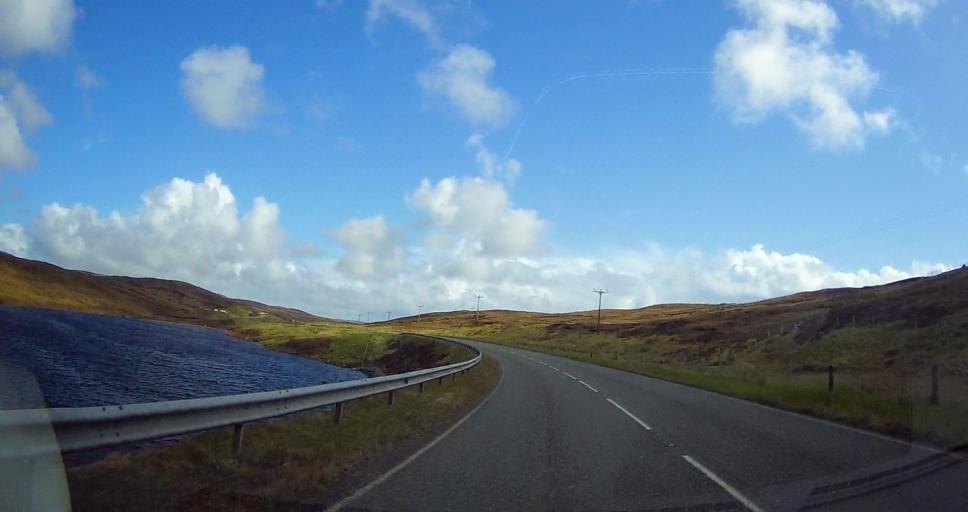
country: GB
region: Scotland
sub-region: Shetland Islands
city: Lerwick
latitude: 60.4412
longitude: -1.3964
